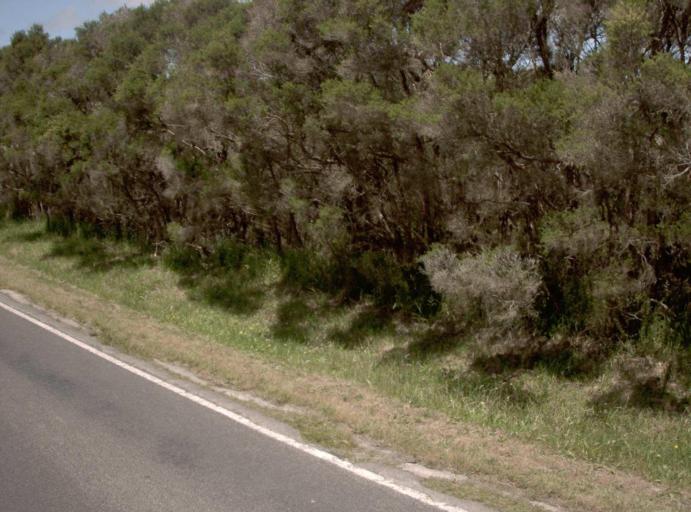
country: AU
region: Victoria
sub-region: Bass Coast
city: North Wonthaggi
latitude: -38.6663
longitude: 146.0237
